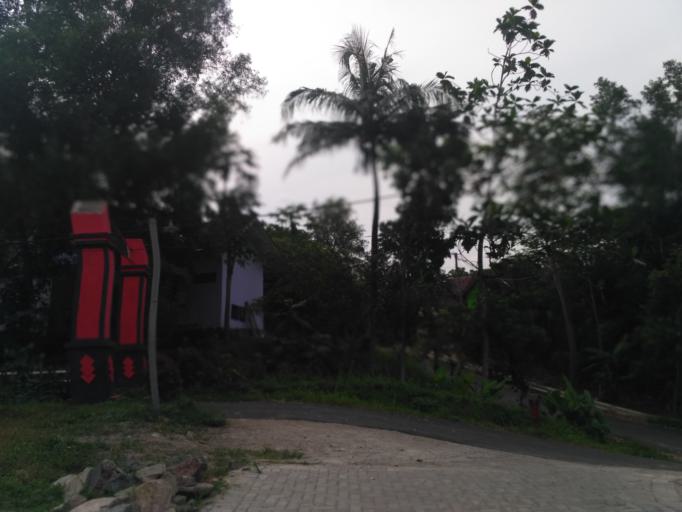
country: ID
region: Central Java
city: Ungaran
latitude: -7.0814
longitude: 110.4268
